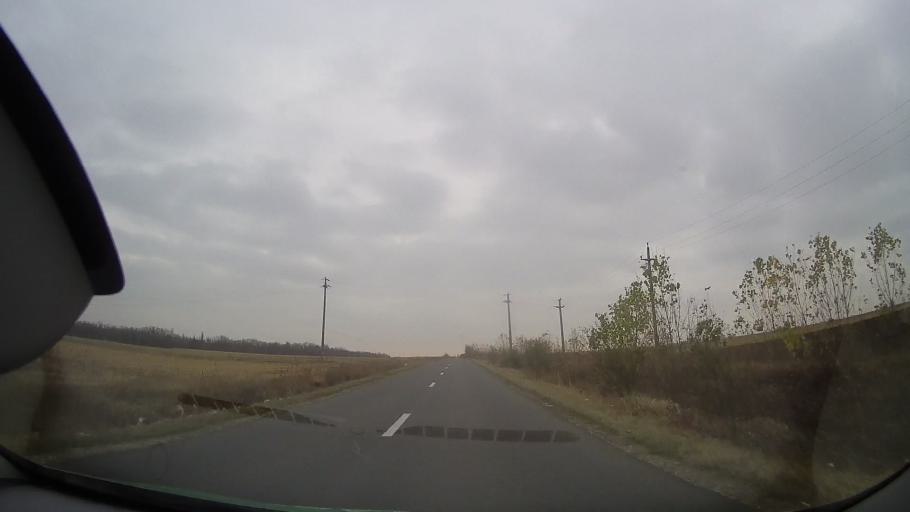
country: RO
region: Ialomita
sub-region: Comuna Manasia
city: Manasia
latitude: 44.7356
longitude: 26.7035
